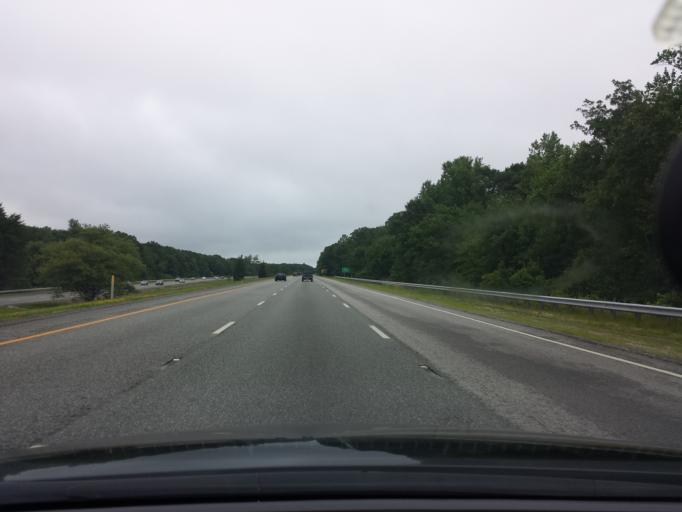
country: US
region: Rhode Island
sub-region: Washington County
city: Hope Valley
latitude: 41.5444
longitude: -71.6757
